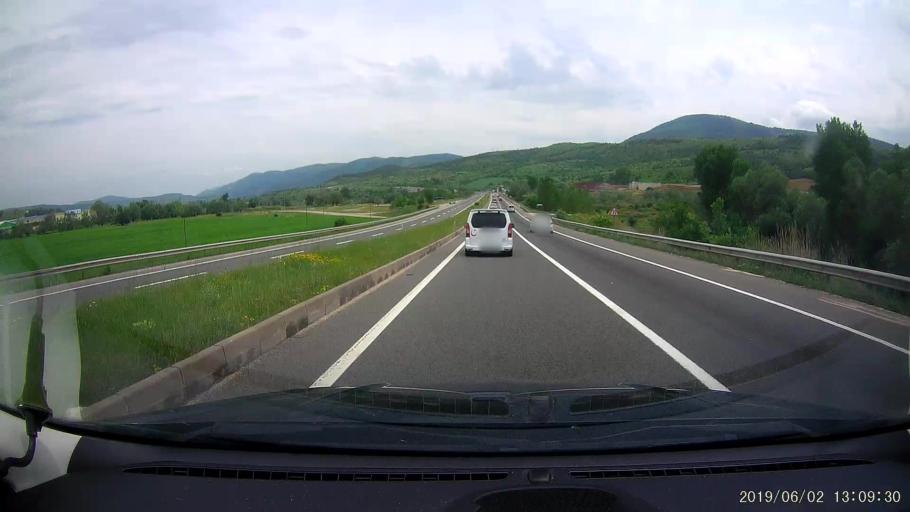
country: TR
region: Karabuk
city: Gozyeri
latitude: 40.8689
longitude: 32.5899
